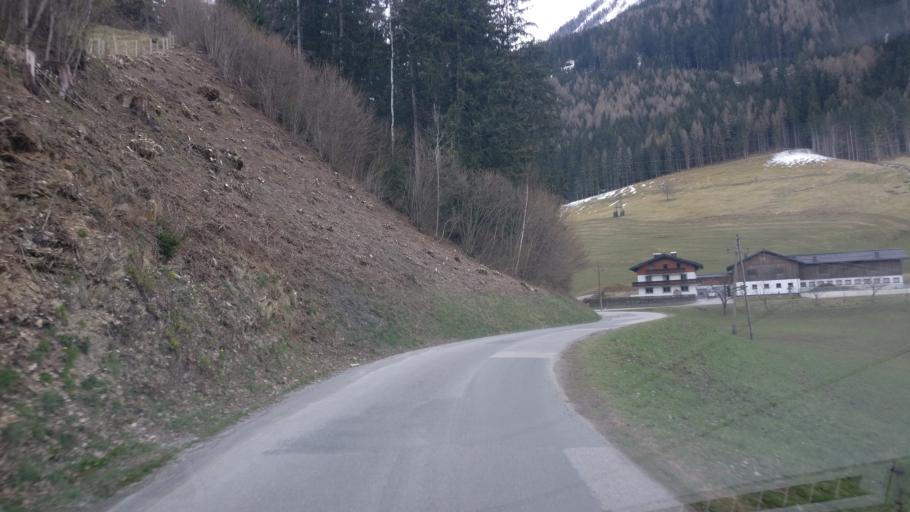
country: AT
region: Salzburg
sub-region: Politischer Bezirk Sankt Johann im Pongau
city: Schwarzach im Pongau
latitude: 47.3095
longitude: 13.1344
